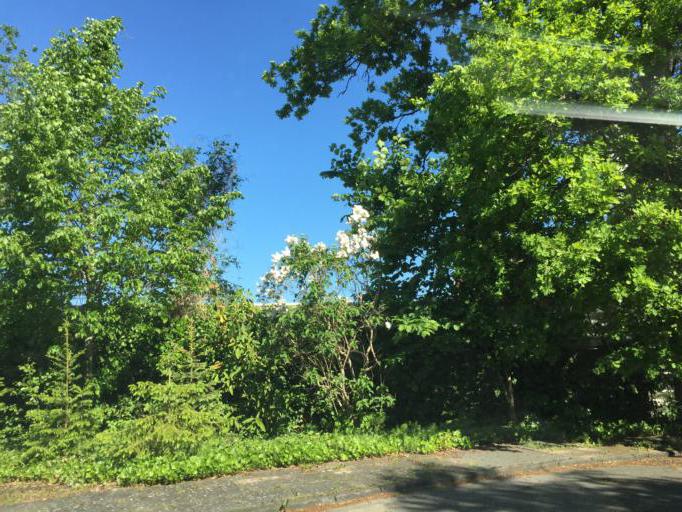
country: DK
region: South Denmark
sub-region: Odense Kommune
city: Odense
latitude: 55.3621
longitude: 10.3801
